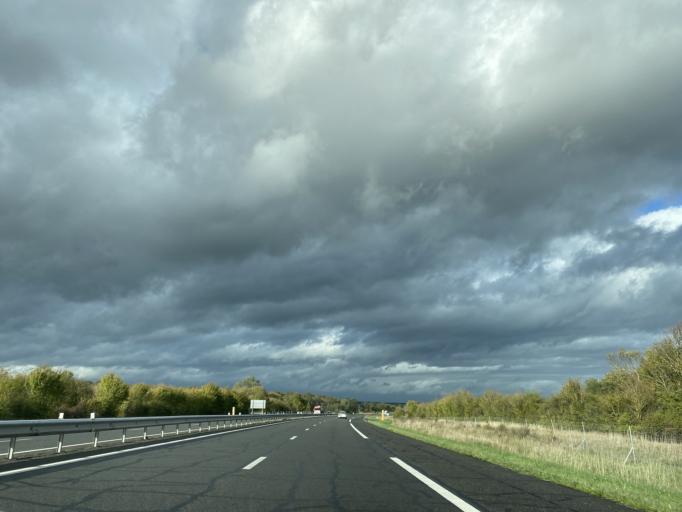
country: FR
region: Centre
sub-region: Departement du Cher
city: Orval
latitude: 46.7667
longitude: 2.4063
